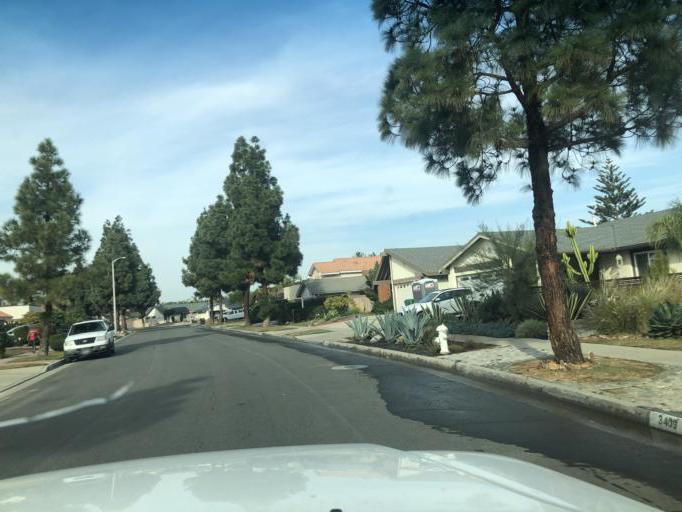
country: US
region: California
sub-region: Orange County
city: Santa Ana
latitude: 33.7012
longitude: -117.8714
